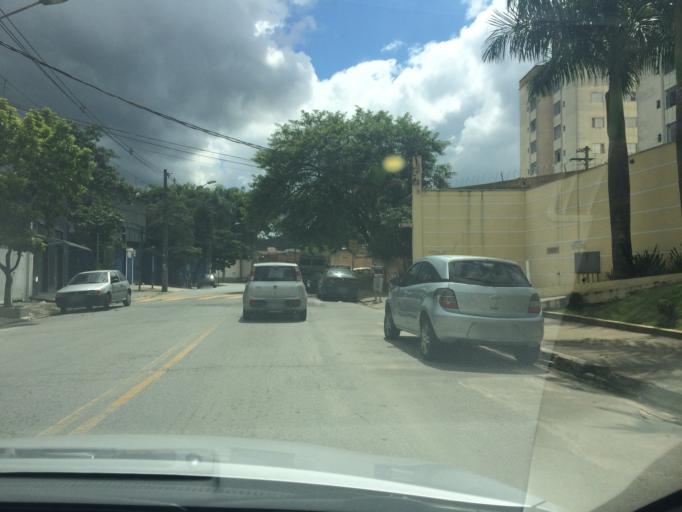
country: BR
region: Sao Paulo
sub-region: Guarulhos
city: Guarulhos
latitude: -23.4360
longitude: -46.5362
